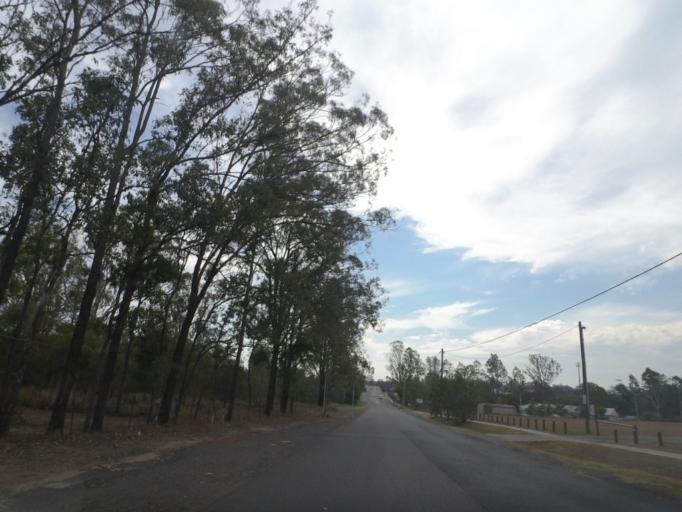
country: AU
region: Queensland
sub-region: Brisbane
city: Richlands
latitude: -27.5931
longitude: 152.9533
